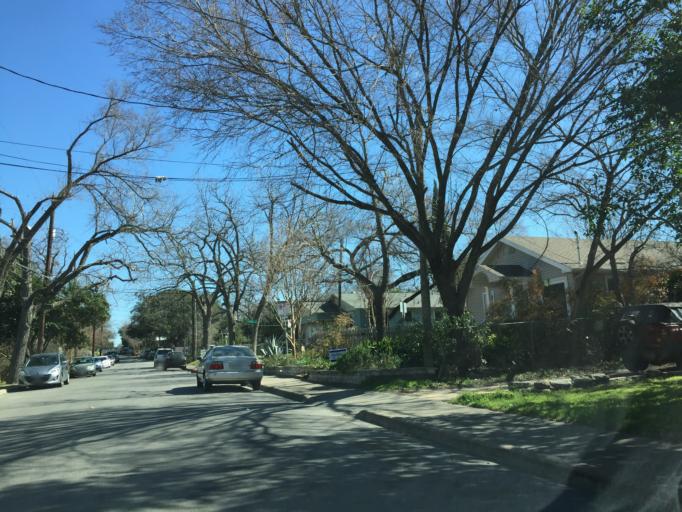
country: US
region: Texas
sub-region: Travis County
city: Austin
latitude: 30.2490
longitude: -97.7539
